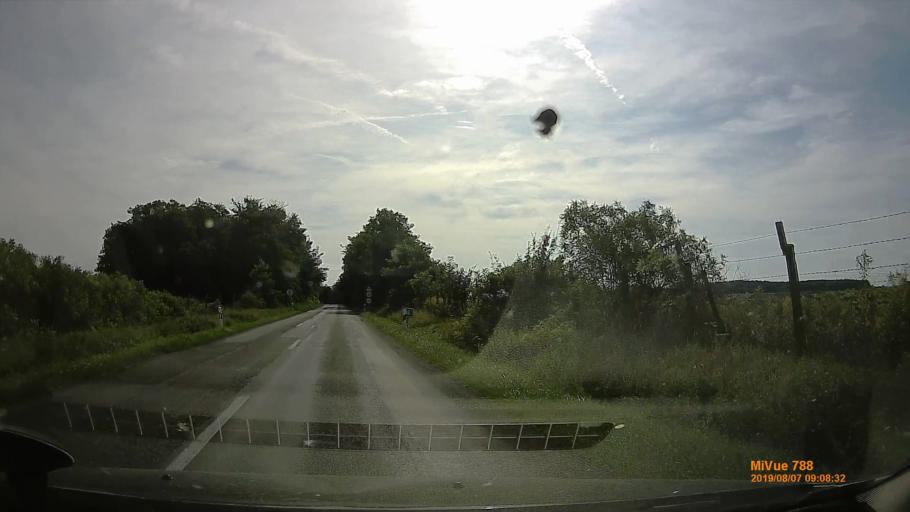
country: HU
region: Zala
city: Pacsa
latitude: 46.7288
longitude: 17.0560
